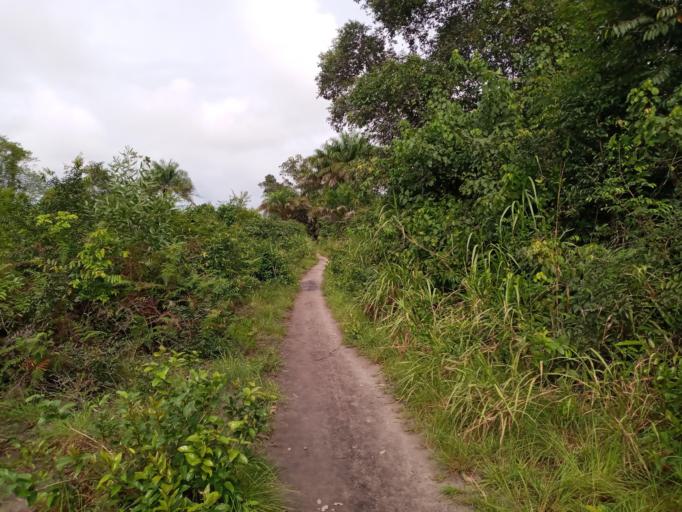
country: SL
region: Southern Province
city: Bonthe
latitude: 7.5187
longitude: -12.5401
